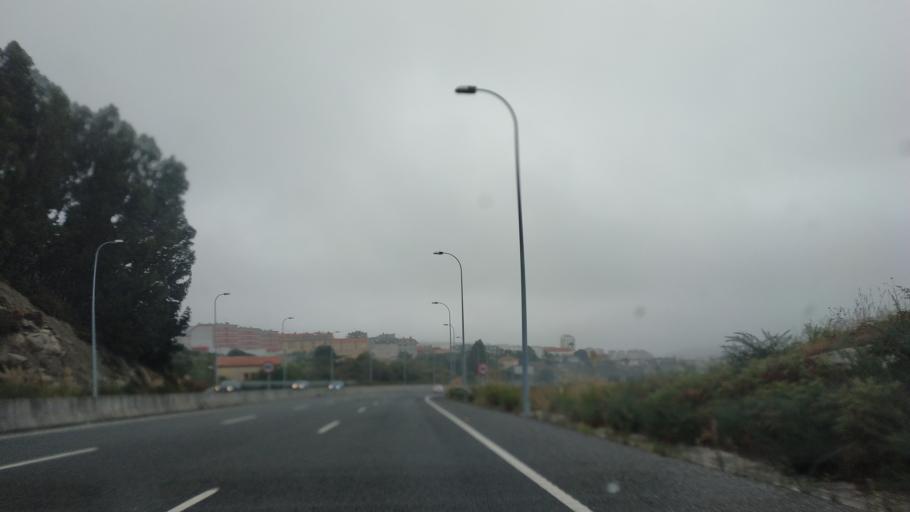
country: ES
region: Galicia
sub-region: Provincia da Coruna
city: A Coruna
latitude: 43.3639
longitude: -8.4322
